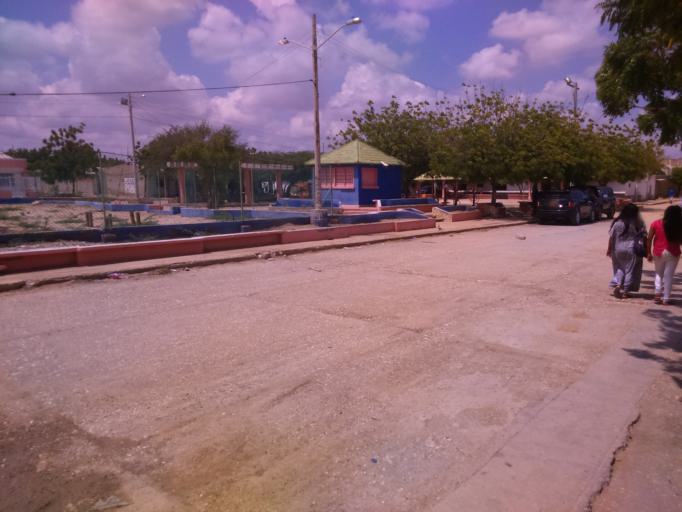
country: CO
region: La Guajira
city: Manaure
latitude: 11.7783
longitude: -72.4442
